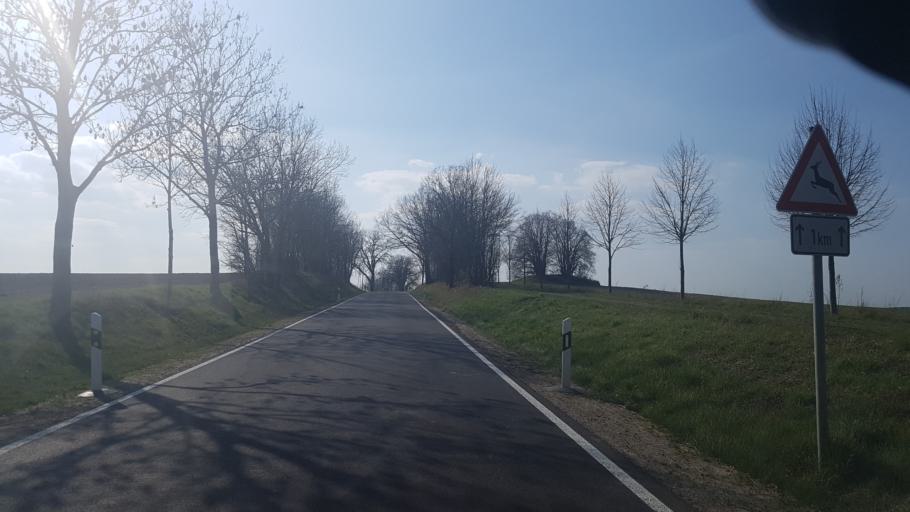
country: DE
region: Brandenburg
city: Gerswalde
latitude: 53.1593
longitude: 13.8410
